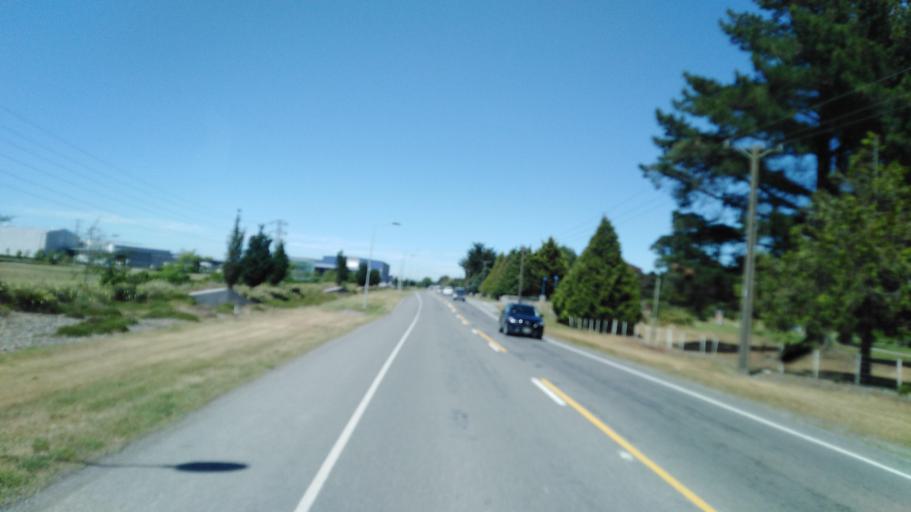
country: NZ
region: Canterbury
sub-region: Selwyn District
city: Prebbleton
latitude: -43.5371
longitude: 172.4946
